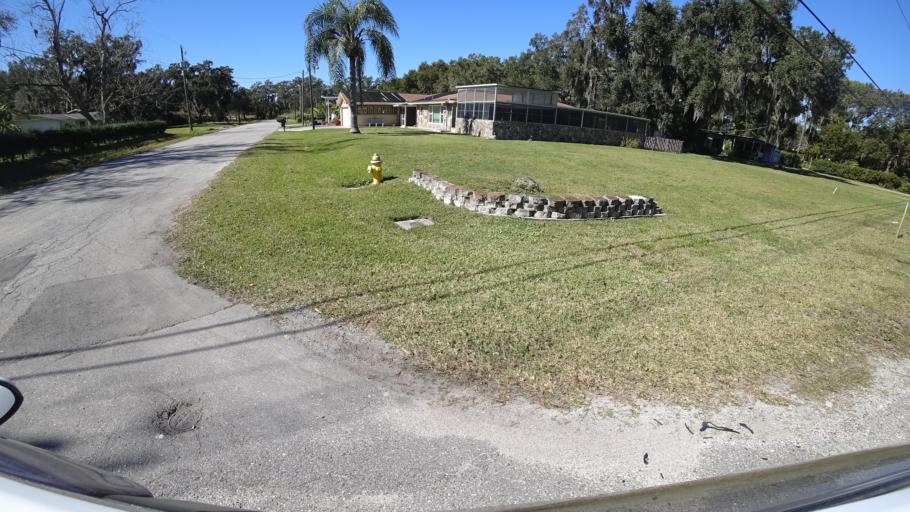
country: US
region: Florida
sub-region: Manatee County
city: Memphis
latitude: 27.5607
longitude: -82.5483
